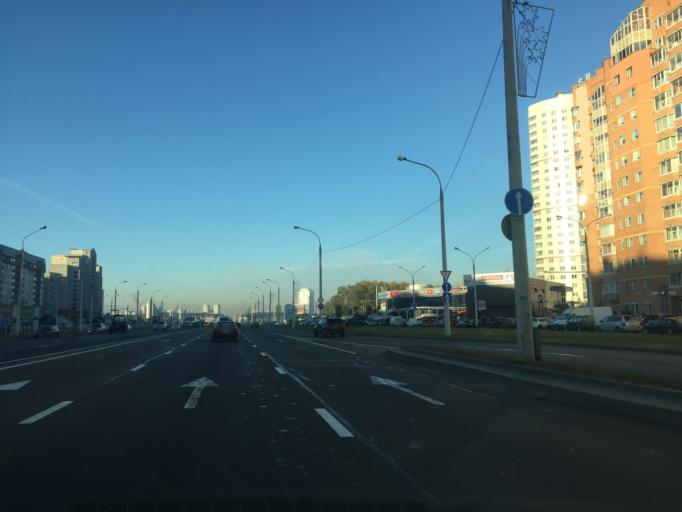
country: BY
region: Minsk
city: Borovlyany
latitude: 53.9467
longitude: 27.6919
